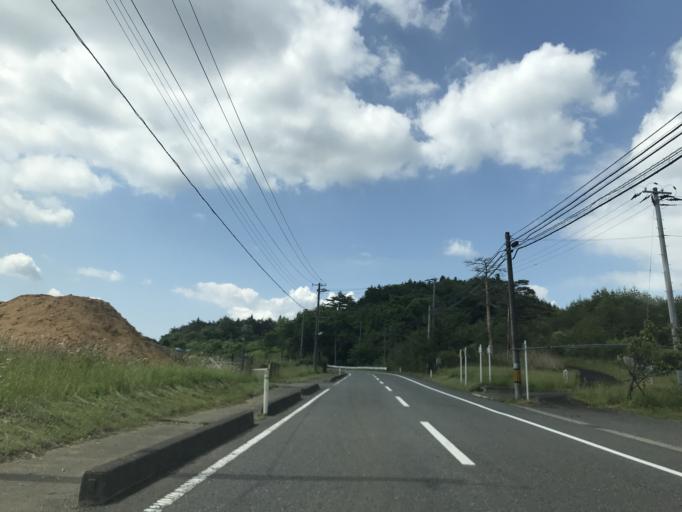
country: JP
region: Miyagi
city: Furukawa
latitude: 38.7639
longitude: 140.9588
